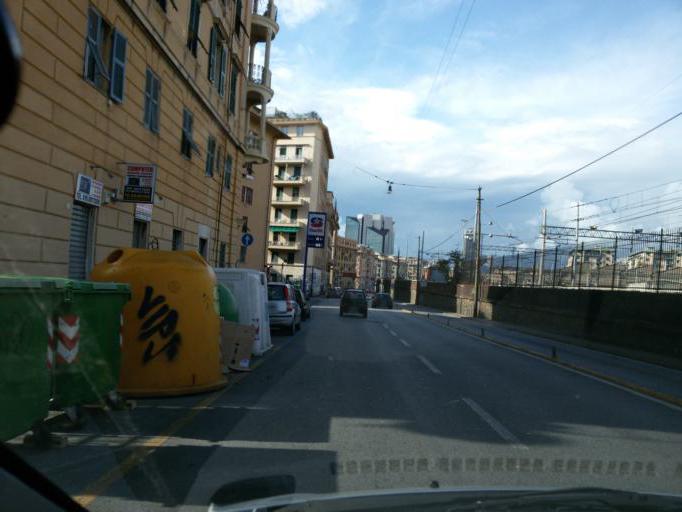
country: IT
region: Liguria
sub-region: Provincia di Genova
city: Genoa
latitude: 44.4047
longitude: 8.9561
